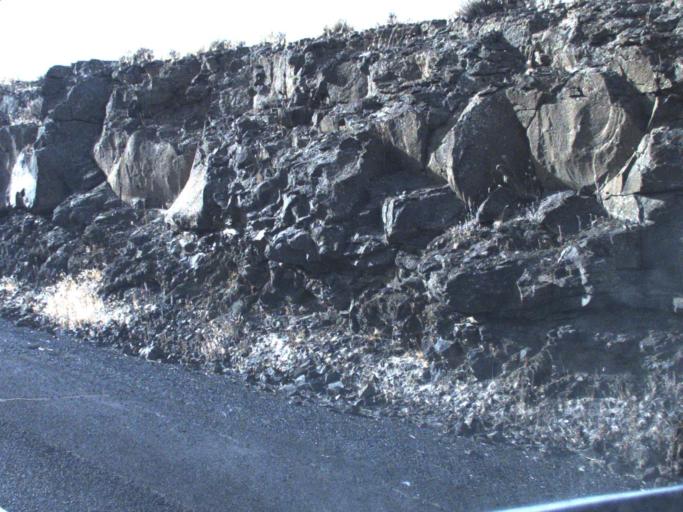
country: US
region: Washington
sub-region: Adams County
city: Ritzville
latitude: 47.3631
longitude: -118.4723
